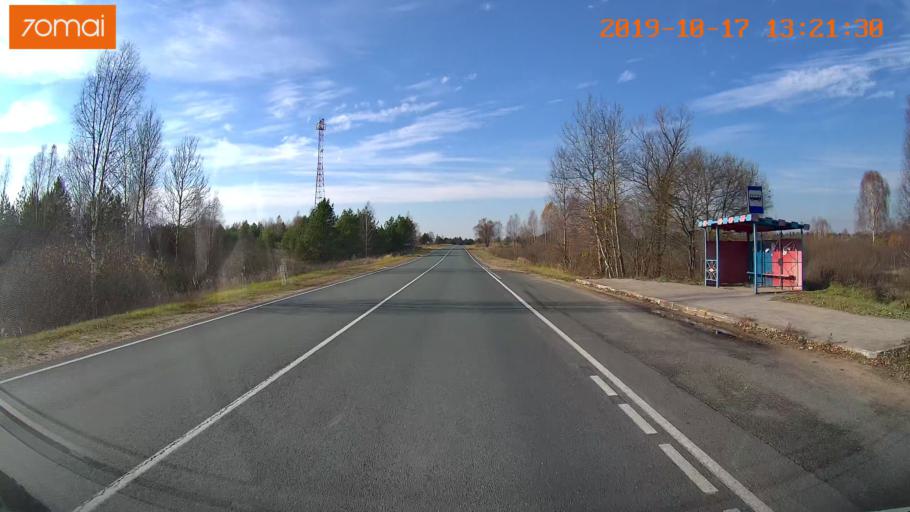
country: RU
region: Rjazan
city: Gus'-Zheleznyy
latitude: 55.0812
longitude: 41.0257
